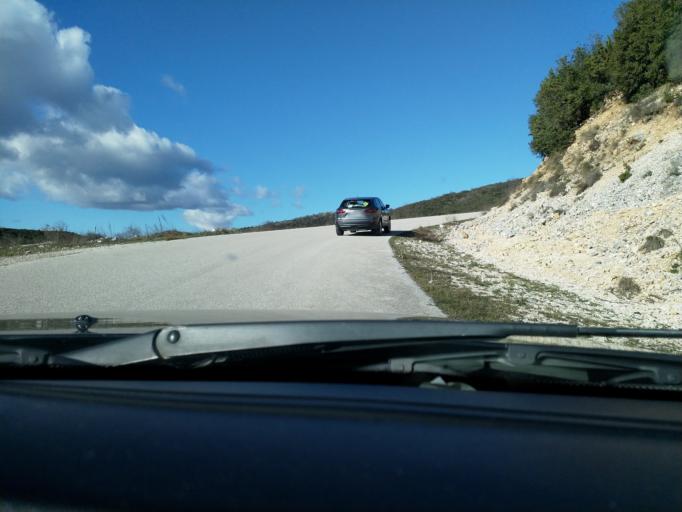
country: GR
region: Epirus
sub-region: Nomos Ioanninon
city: Kalpaki
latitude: 39.8999
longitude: 20.6702
